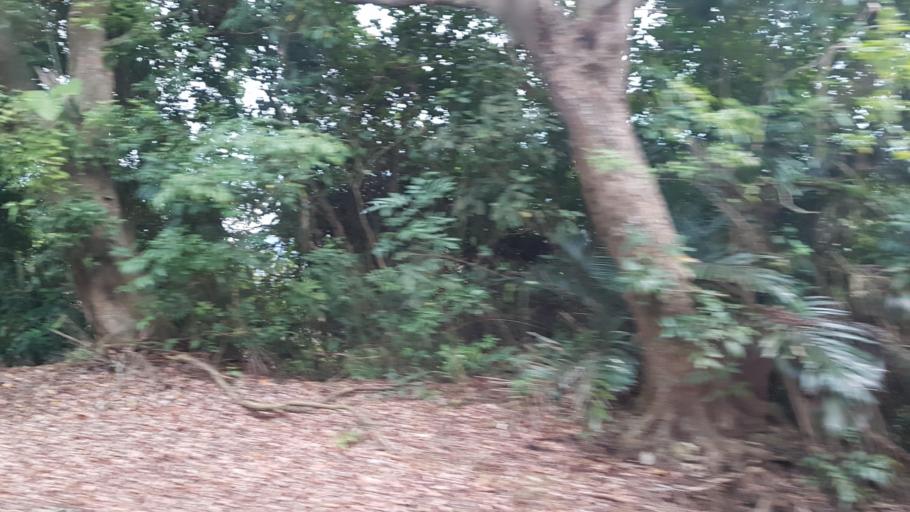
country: TW
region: Taiwan
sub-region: Chiayi
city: Jiayi Shi
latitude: 23.3260
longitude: 120.4879
